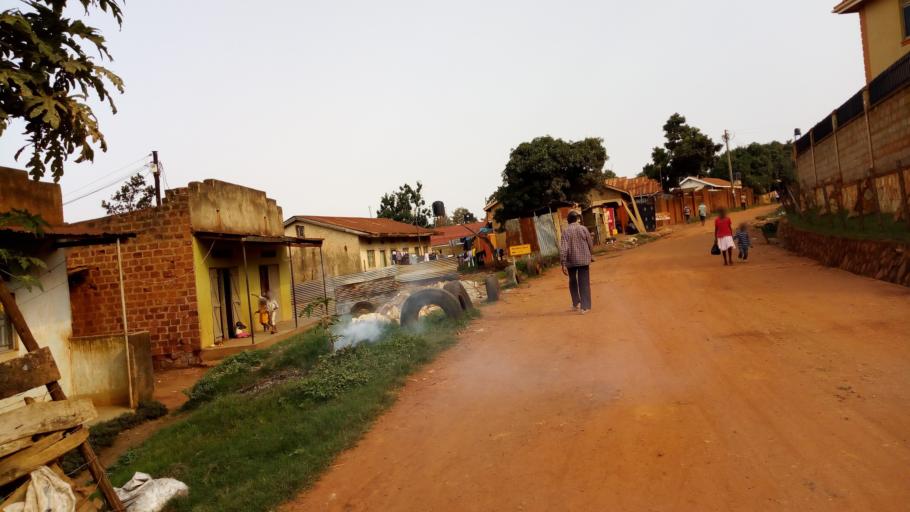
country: UG
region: Central Region
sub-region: Wakiso District
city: Kireka
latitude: 0.3116
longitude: 32.6501
